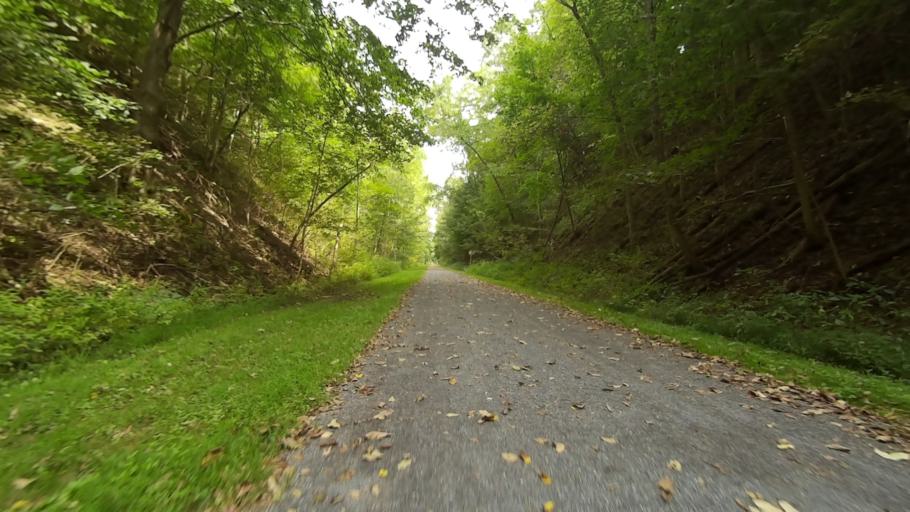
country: US
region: Pennsylvania
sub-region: Blair County
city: Williamsburg
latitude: 40.5274
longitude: -78.1696
